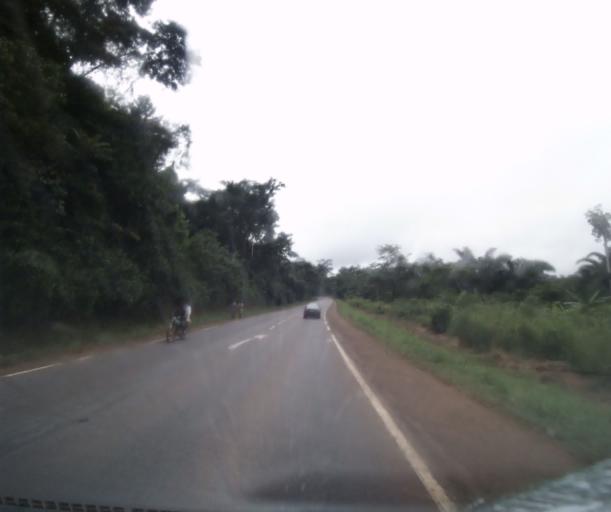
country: CM
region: Centre
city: Mbankomo
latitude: 3.7821
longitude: 11.2489
